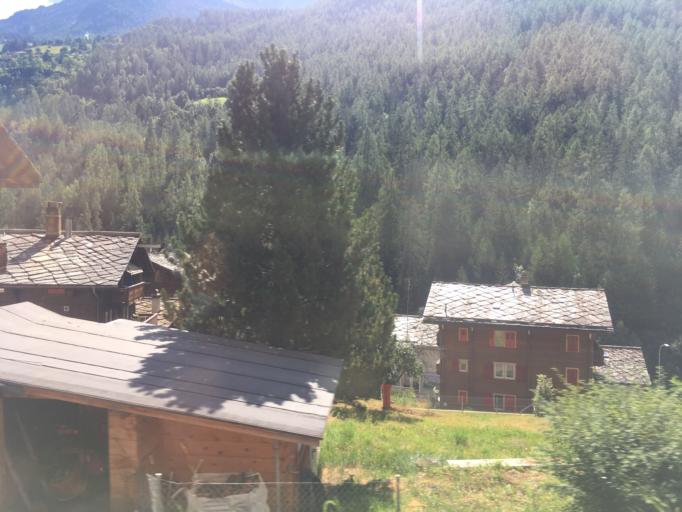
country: CH
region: Valais
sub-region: Visp District
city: Sankt Niklaus
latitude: 46.1753
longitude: 7.8006
